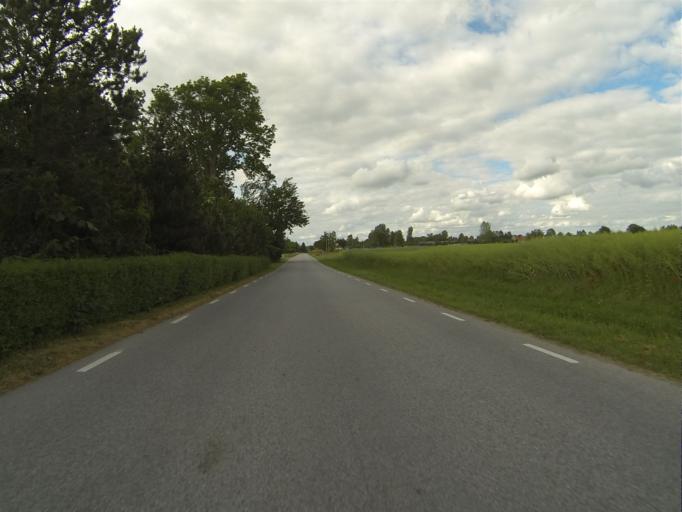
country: SE
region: Skane
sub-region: Staffanstorps Kommun
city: Staffanstorp
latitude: 55.6243
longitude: 13.2196
